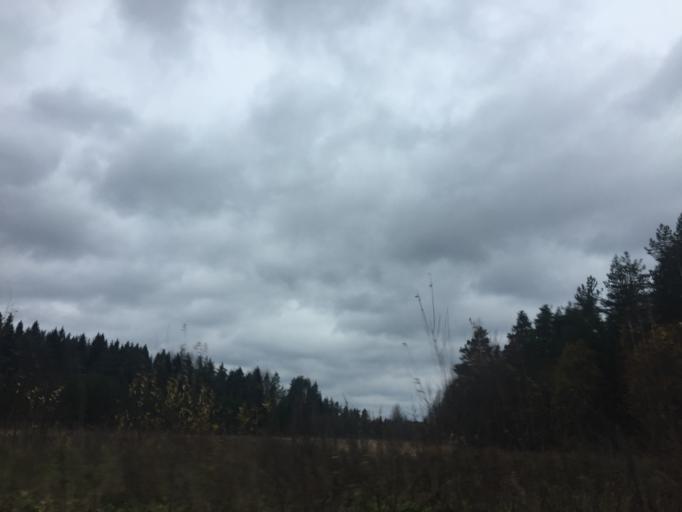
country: RU
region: Republic of Karelia
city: Lakhdenpokh'ya
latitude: 61.4296
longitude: 30.1265
